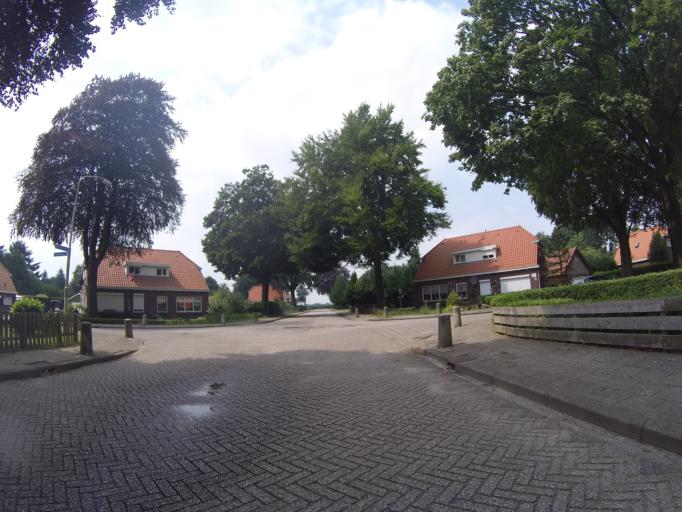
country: NL
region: Drenthe
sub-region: Gemeente Emmen
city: Emmer-Compascuum
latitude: 52.8623
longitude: 7.0789
